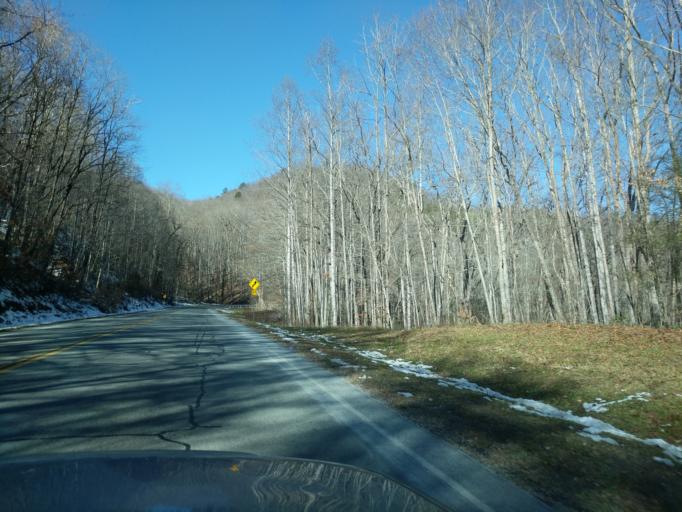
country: US
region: Georgia
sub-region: Rabun County
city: Clayton
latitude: 34.8763
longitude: -83.5769
